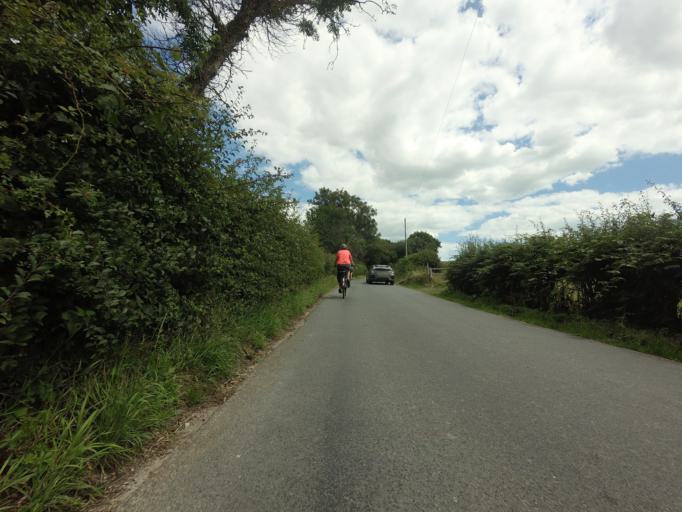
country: GB
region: England
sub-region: East Sussex
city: Hailsham
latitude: 50.8351
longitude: 0.2882
